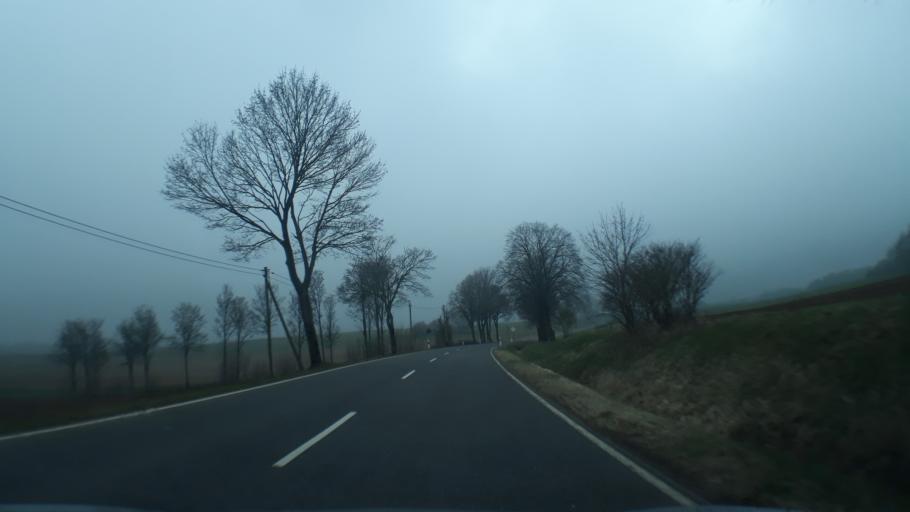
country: DE
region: North Rhine-Westphalia
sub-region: Regierungsbezirk Koln
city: Nettersheim
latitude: 50.4913
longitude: 6.5847
